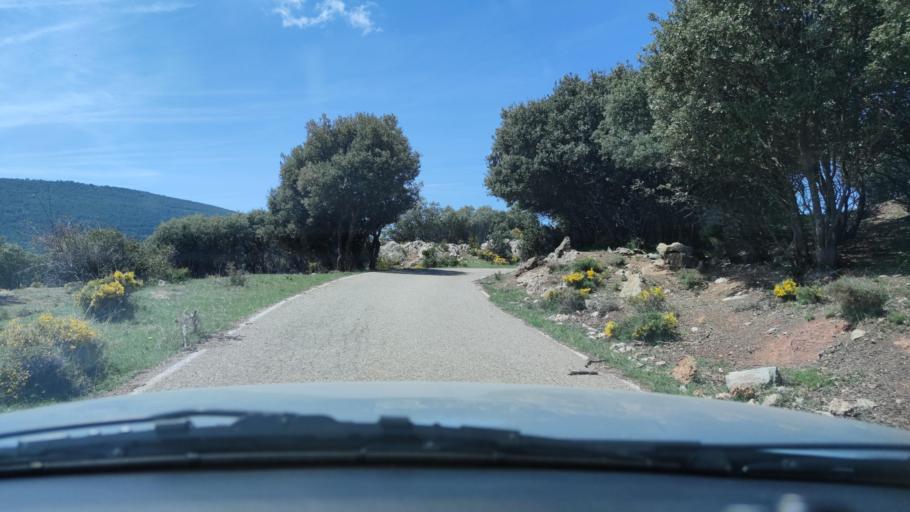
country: ES
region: Catalonia
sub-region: Provincia de Lleida
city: Sort
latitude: 42.3045
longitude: 1.1151
